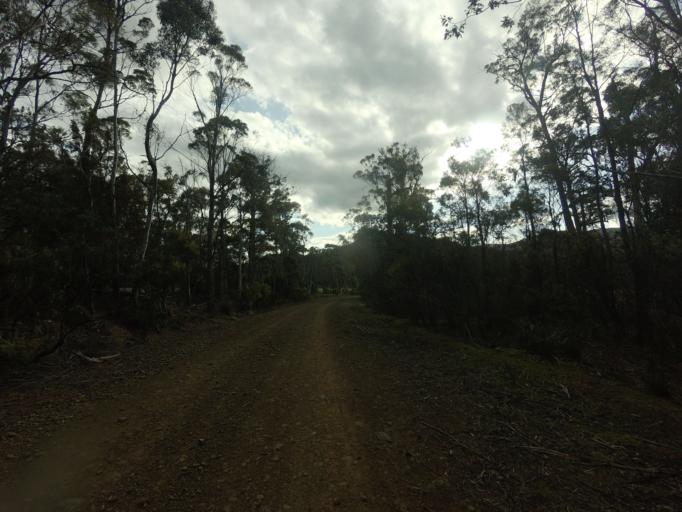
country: AU
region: Tasmania
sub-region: Break O'Day
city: St Helens
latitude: -41.8629
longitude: 148.0227
